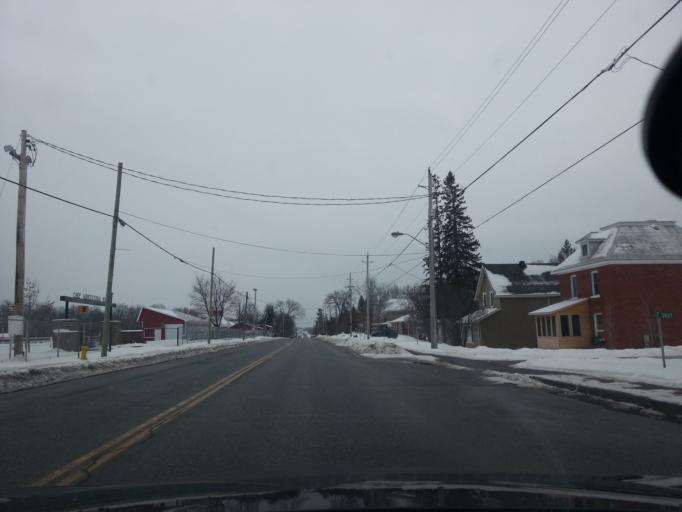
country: CA
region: Ontario
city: Bells Corners
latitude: 45.3481
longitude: -76.0403
